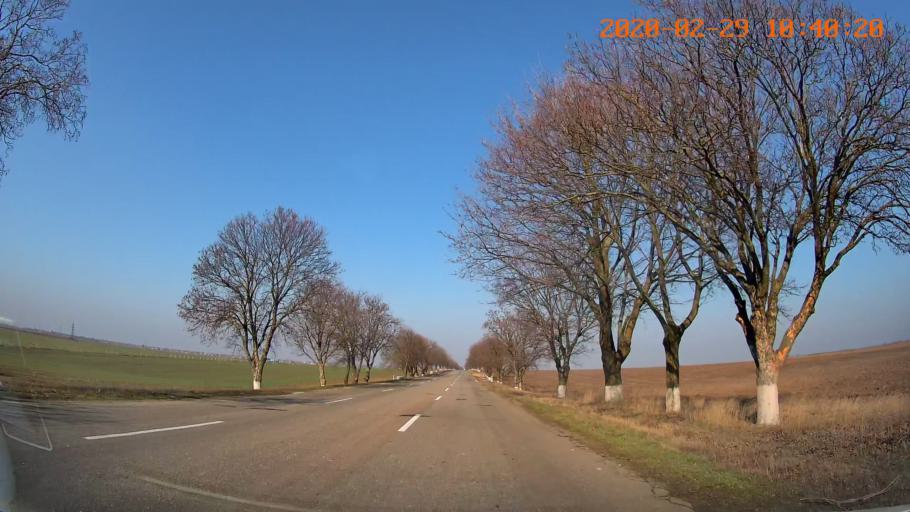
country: MD
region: Anenii Noi
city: Varnita
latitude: 47.0320
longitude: 29.4413
